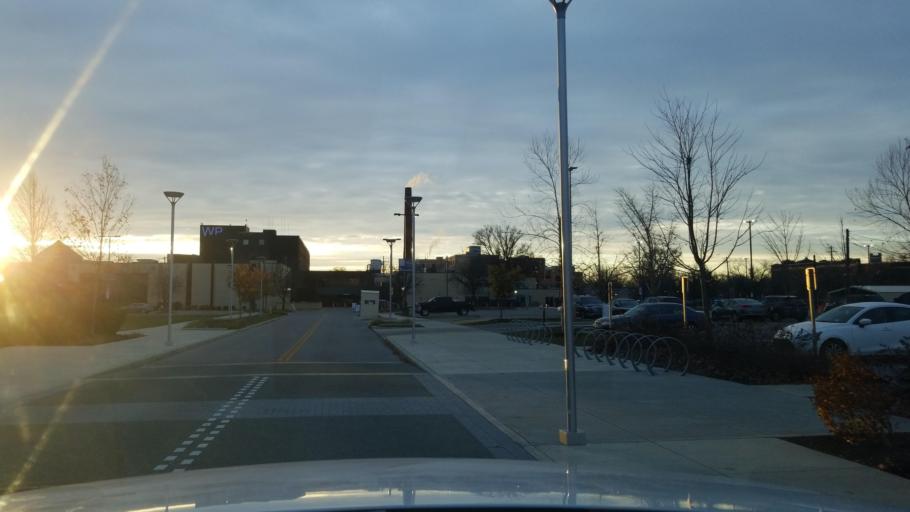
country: US
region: Indiana
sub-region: Vanderburgh County
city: Evansville
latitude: 37.9703
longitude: -87.5685
